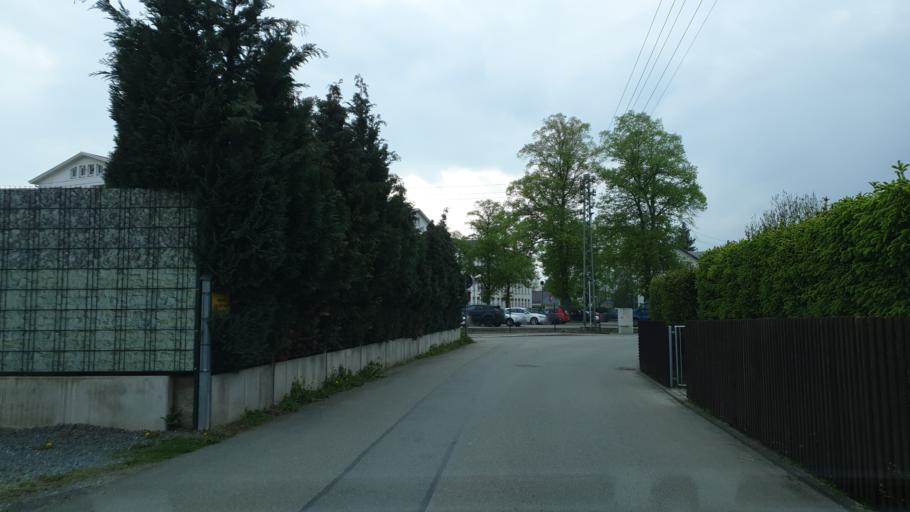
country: DE
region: Saxony
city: Oberlungwitz
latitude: 50.7824
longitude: 12.7052
